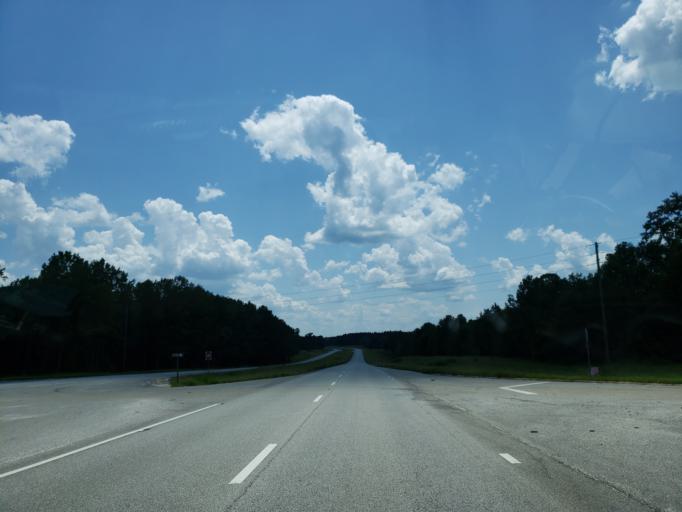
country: US
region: Mississippi
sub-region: Greene County
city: Leakesville
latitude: 31.3568
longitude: -88.5012
